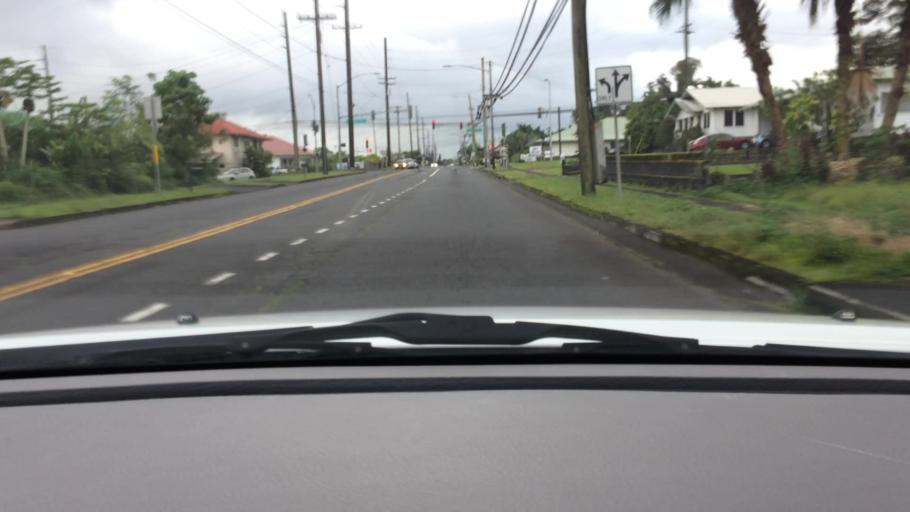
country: US
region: Hawaii
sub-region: Hawaii County
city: Hilo
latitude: 19.7070
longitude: -155.0774
